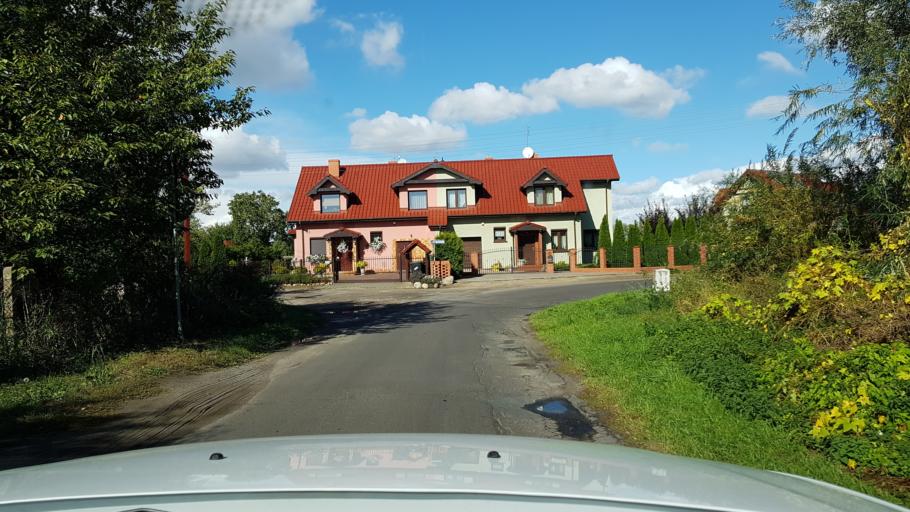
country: PL
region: West Pomeranian Voivodeship
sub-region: Powiat gryfinski
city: Gryfino
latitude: 53.2761
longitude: 14.4937
